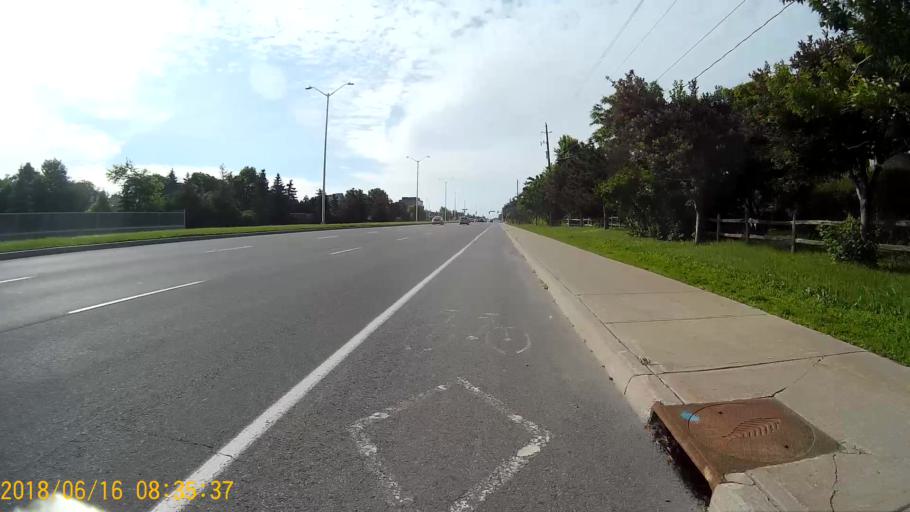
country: CA
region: Ontario
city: Bells Corners
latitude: 45.3528
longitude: -75.9300
